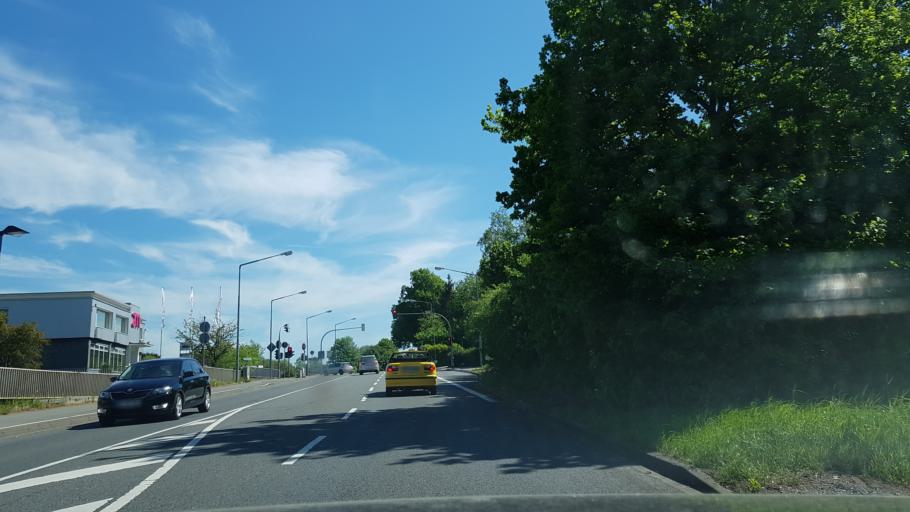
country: DE
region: North Rhine-Westphalia
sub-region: Regierungsbezirk Dusseldorf
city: Heiligenhaus
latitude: 51.2966
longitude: 6.9304
